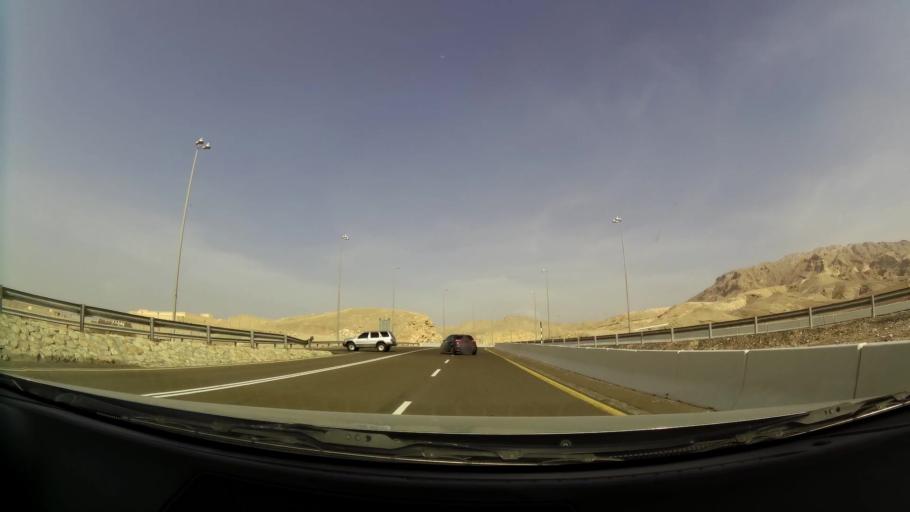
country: AE
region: Abu Dhabi
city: Al Ain
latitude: 24.1117
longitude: 55.7552
